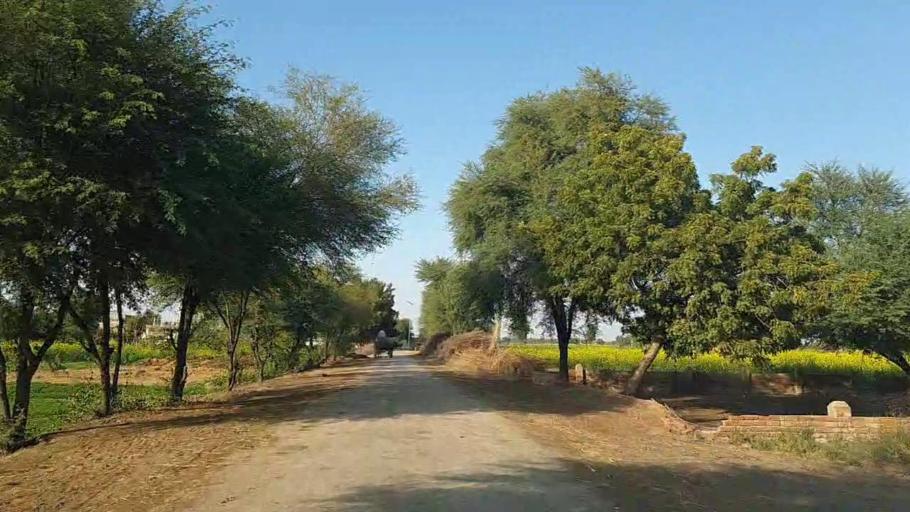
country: PK
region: Sindh
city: Shahpur Chakar
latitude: 26.1962
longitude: 68.6335
